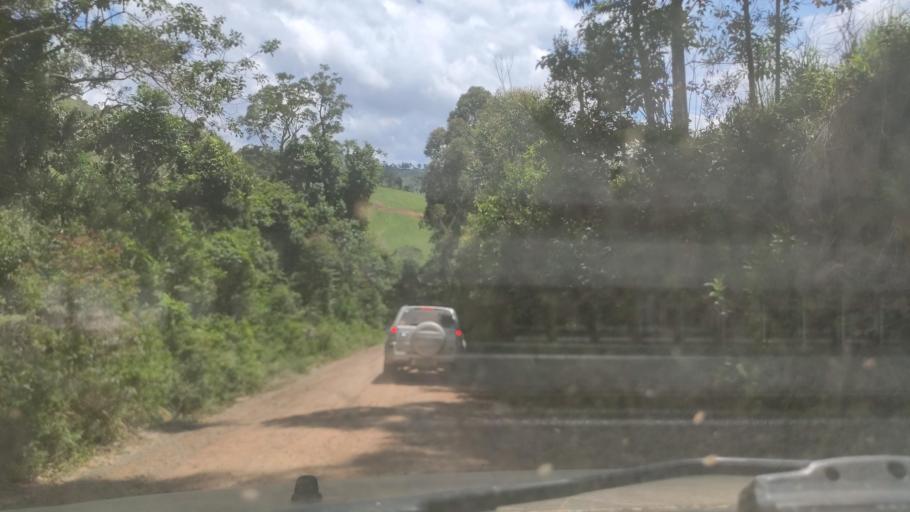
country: BR
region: Minas Gerais
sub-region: Cambui
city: Cambui
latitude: -22.6846
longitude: -45.9744
